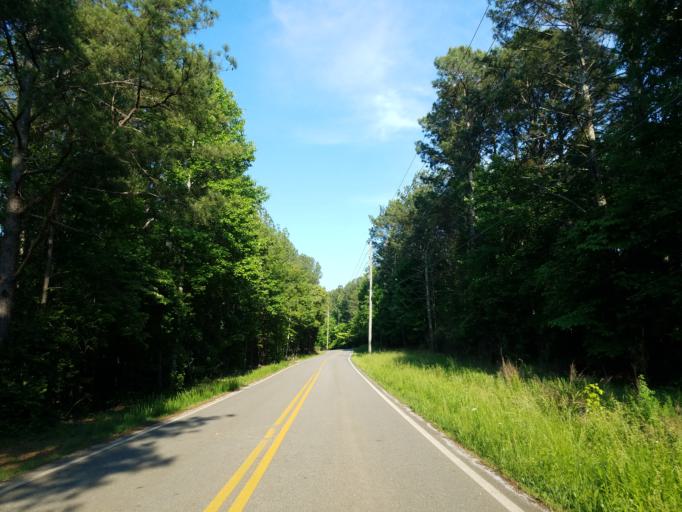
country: US
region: Georgia
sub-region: Pickens County
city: Nelson
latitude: 34.3719
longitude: -84.3306
